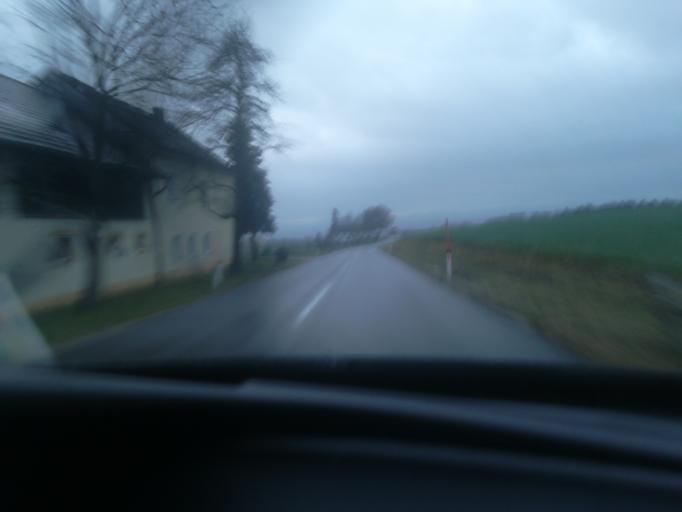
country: AT
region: Upper Austria
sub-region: Politischer Bezirk Perg
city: Perg
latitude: 48.2797
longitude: 14.6309
